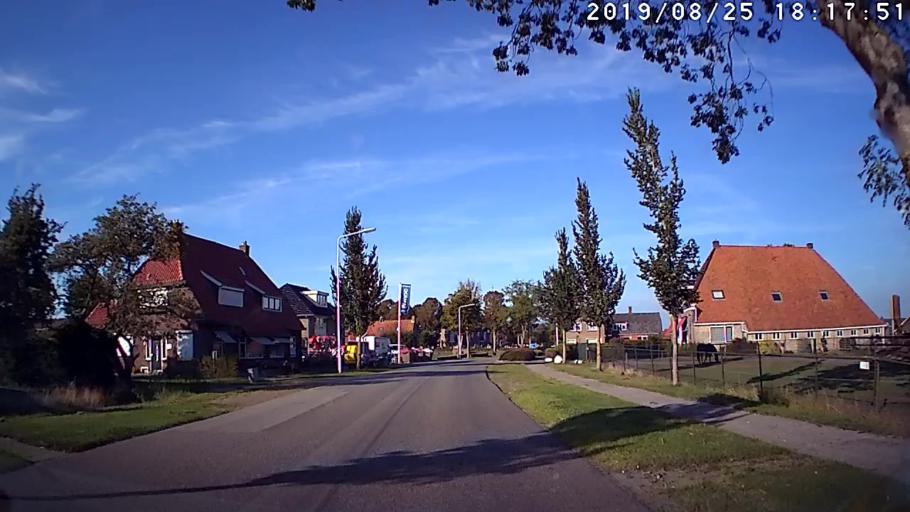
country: NL
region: Friesland
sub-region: Gemeente Gaasterlan-Sleat
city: Balk
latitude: 52.8688
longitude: 5.5955
